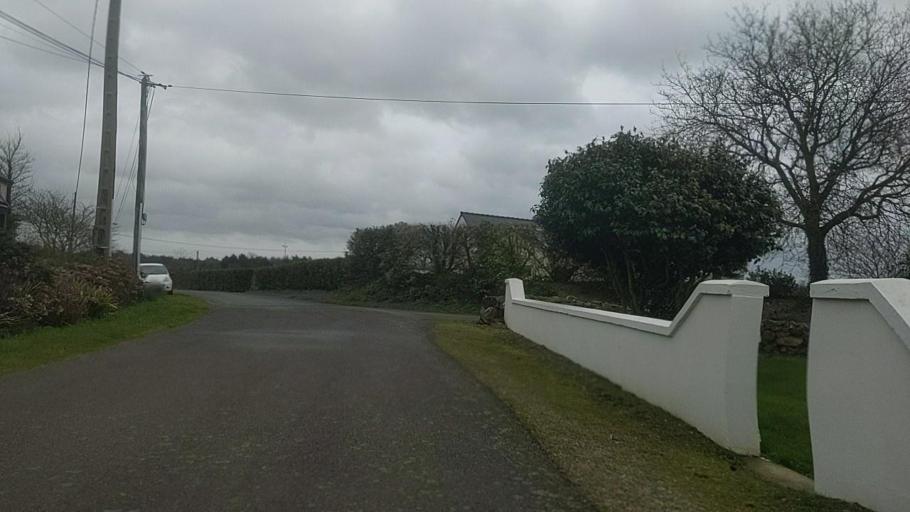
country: FR
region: Brittany
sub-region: Departement des Cotes-d'Armor
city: Tredarzec
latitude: 48.8203
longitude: -3.1933
